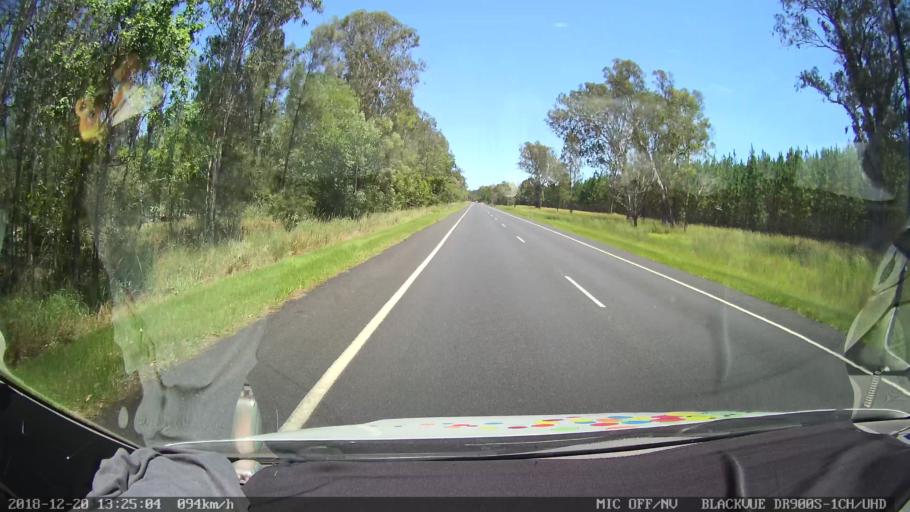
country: AU
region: New South Wales
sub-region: Richmond Valley
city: Casino
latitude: -29.1258
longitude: 152.9978
